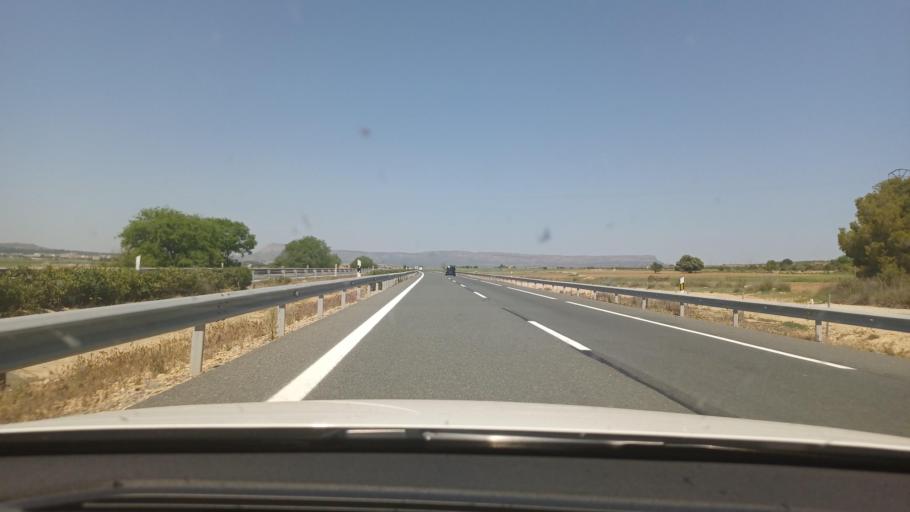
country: ES
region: Castille-La Mancha
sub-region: Provincia de Albacete
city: Almansa
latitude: 38.8568
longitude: -1.0308
